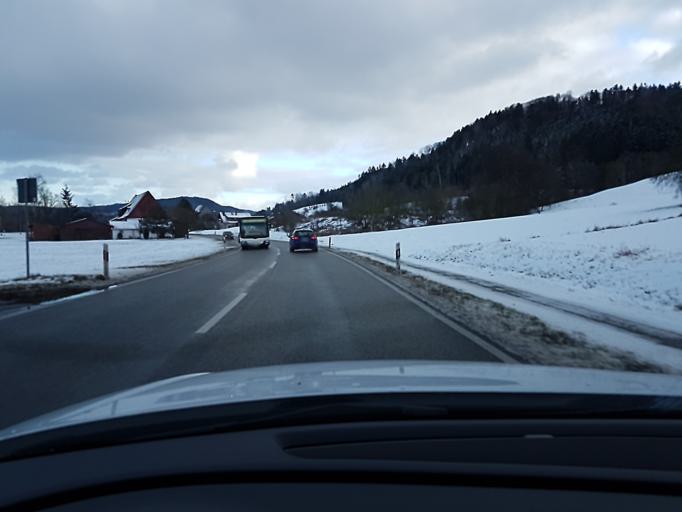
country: DE
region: Baden-Wuerttemberg
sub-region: Regierungsbezirk Stuttgart
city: Murrhardt
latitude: 48.9728
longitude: 9.6127
